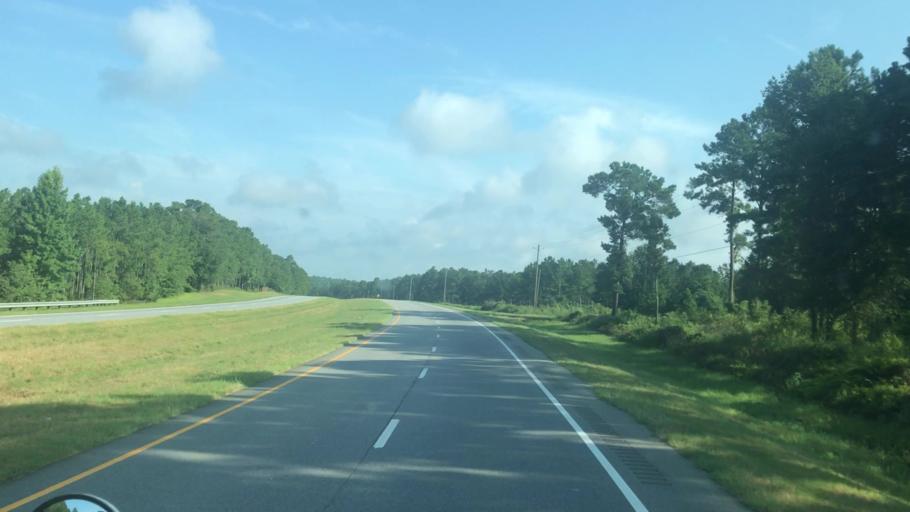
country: US
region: Georgia
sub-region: Decatur County
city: Bainbridge
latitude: 30.8344
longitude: -84.5298
